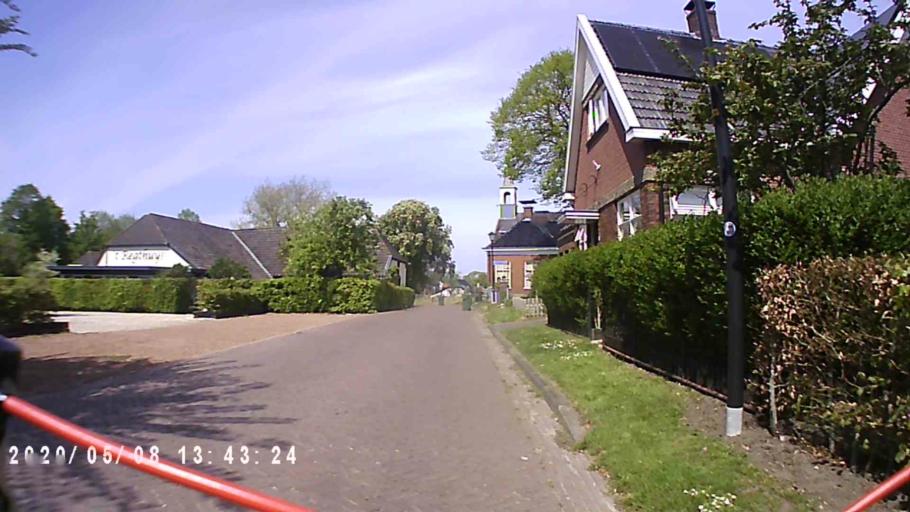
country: NL
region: Groningen
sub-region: Gemeente Appingedam
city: Appingedam
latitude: 53.3229
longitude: 6.7863
